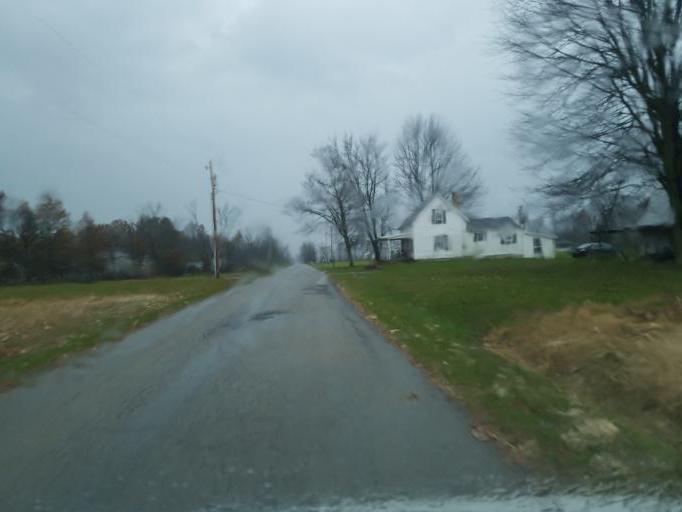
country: US
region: Ohio
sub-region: Morrow County
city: Cardington
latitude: 40.4620
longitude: -82.8709
